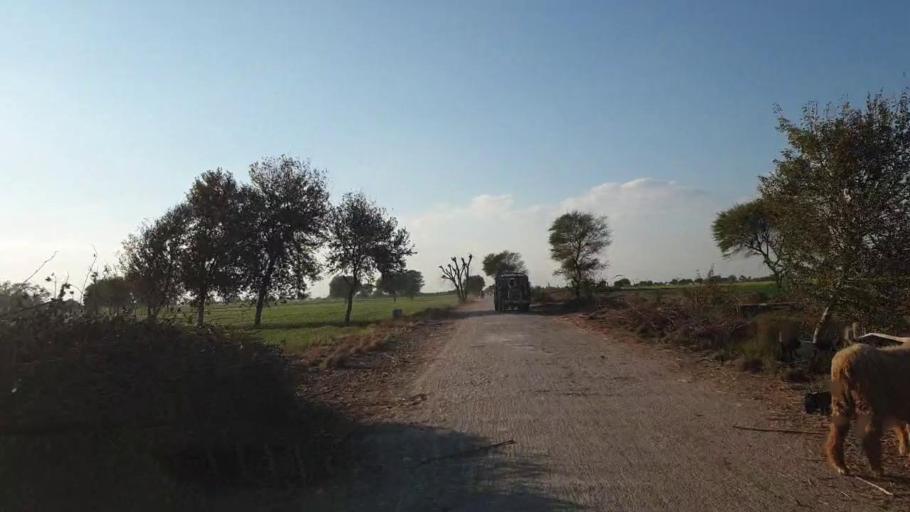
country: PK
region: Sindh
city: Shahpur Chakar
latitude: 26.1379
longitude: 68.5556
